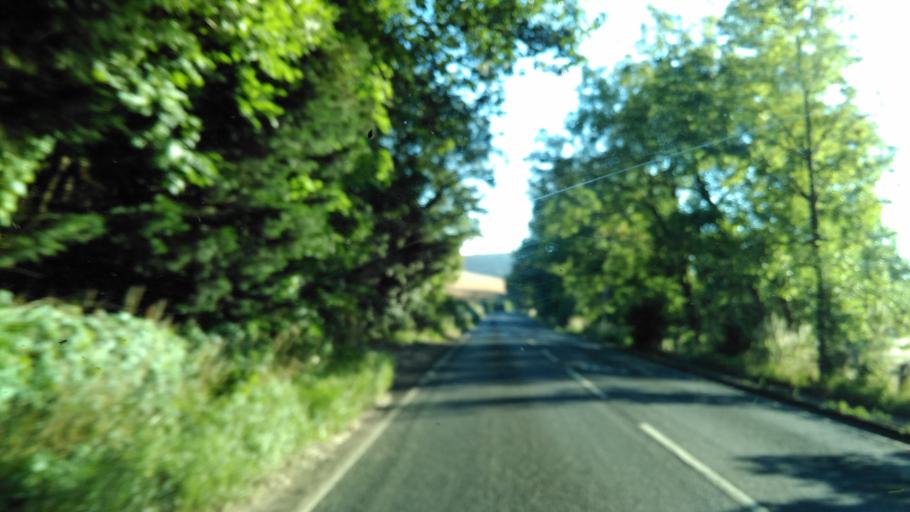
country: GB
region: England
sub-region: Kent
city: Chartham
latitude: 51.2558
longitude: 0.9933
